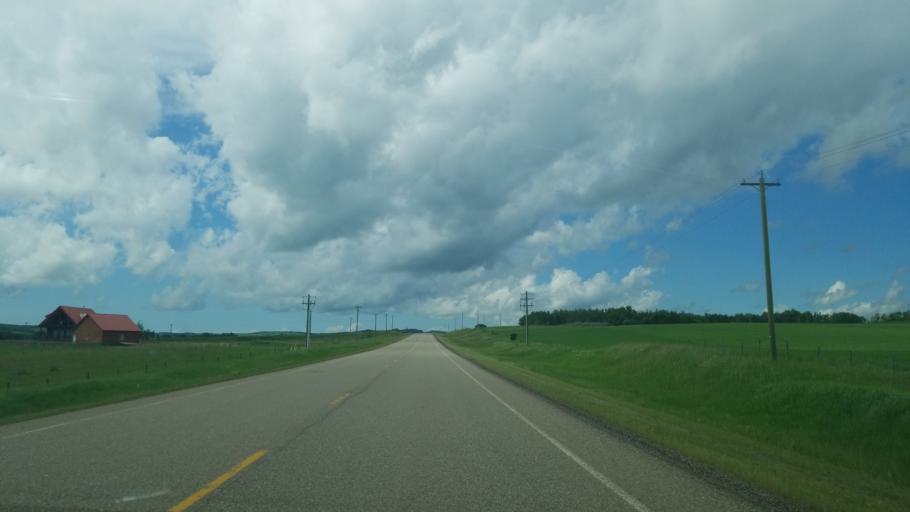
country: CA
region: Saskatchewan
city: Lloydminster
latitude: 53.1617
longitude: -110.1703
